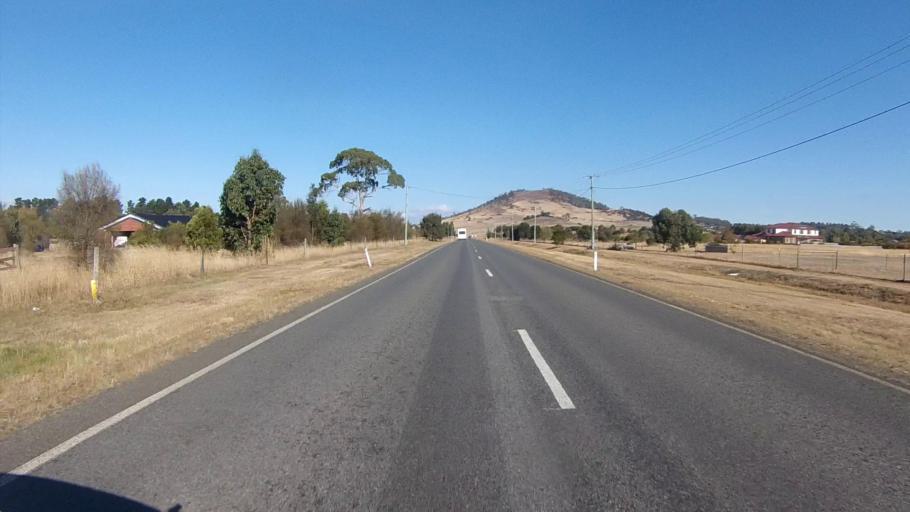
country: AU
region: Tasmania
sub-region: Clarence
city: Seven Mile Beach
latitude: -42.8548
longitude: 147.4883
